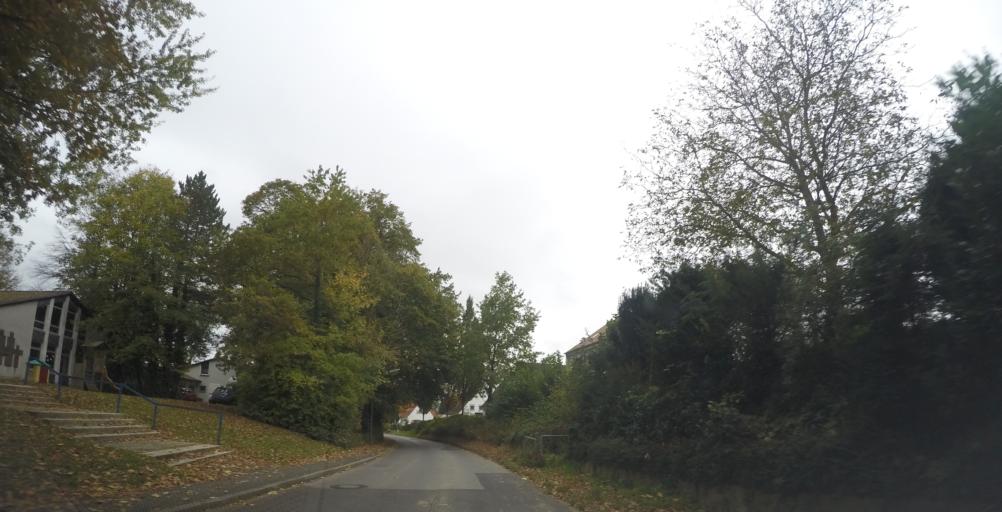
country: DE
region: North Rhine-Westphalia
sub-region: Regierungsbezirk Arnsberg
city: Unna
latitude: 51.4814
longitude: 7.6962
